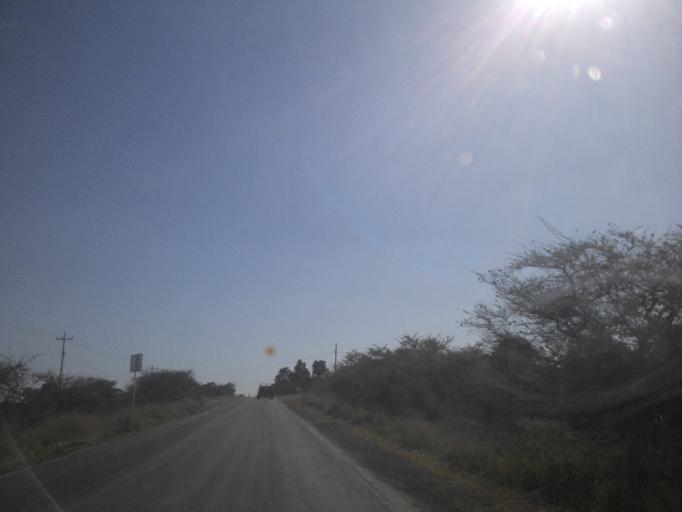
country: MX
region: Jalisco
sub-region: Arandas
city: Santiaguito (Santiaguito de Velazquez)
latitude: 20.7559
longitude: -102.2981
